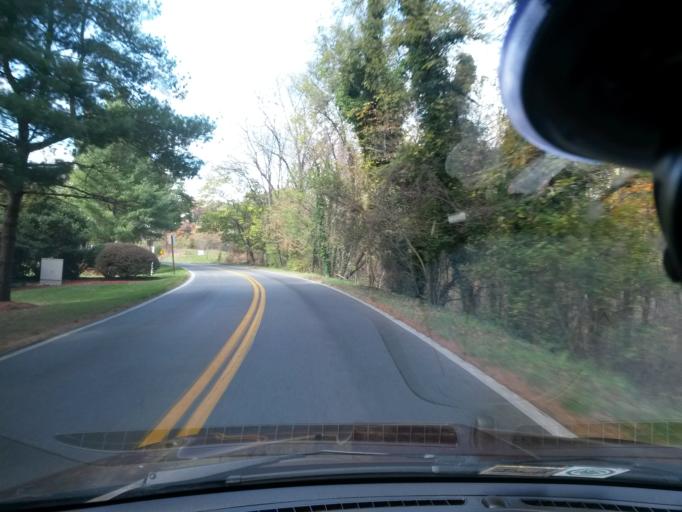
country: US
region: Virginia
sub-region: Roanoke County
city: Cave Spring
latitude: 37.2361
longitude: -79.9845
